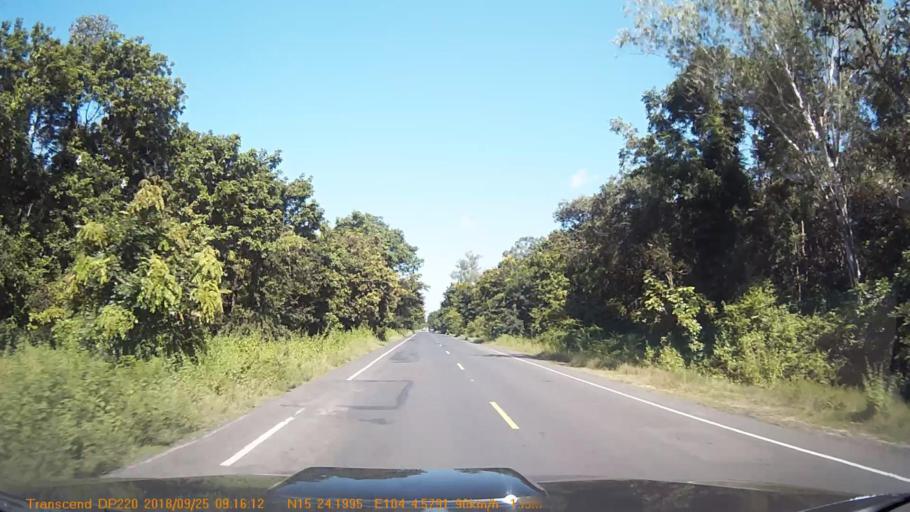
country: TH
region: Sisaket
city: Sila Lat
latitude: 15.4031
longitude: 104.0766
